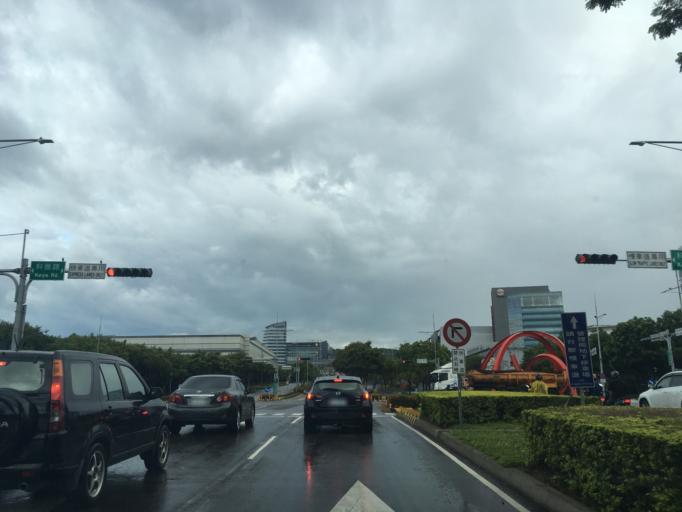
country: TW
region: Taiwan
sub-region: Taichung City
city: Taichung
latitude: 24.2082
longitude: 120.6199
